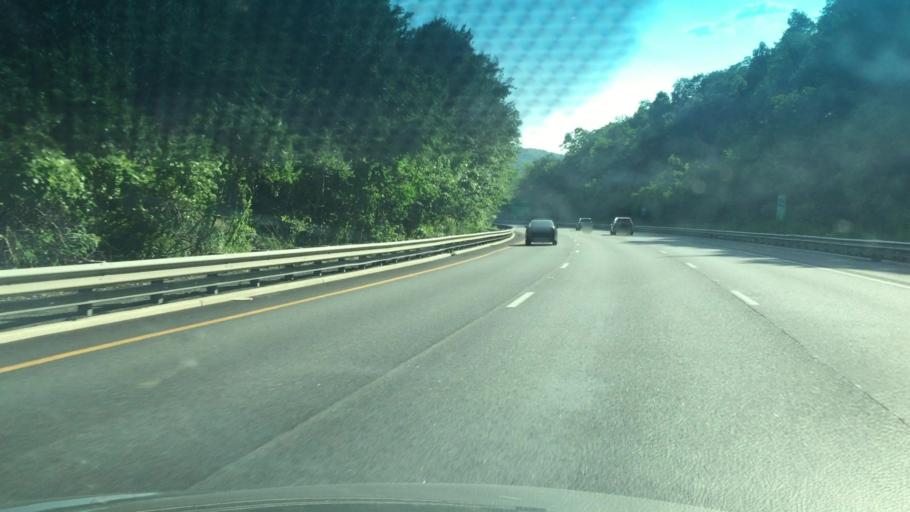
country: US
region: New Jersey
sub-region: Warren County
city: Hackettstown
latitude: 40.9230
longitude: -74.8002
